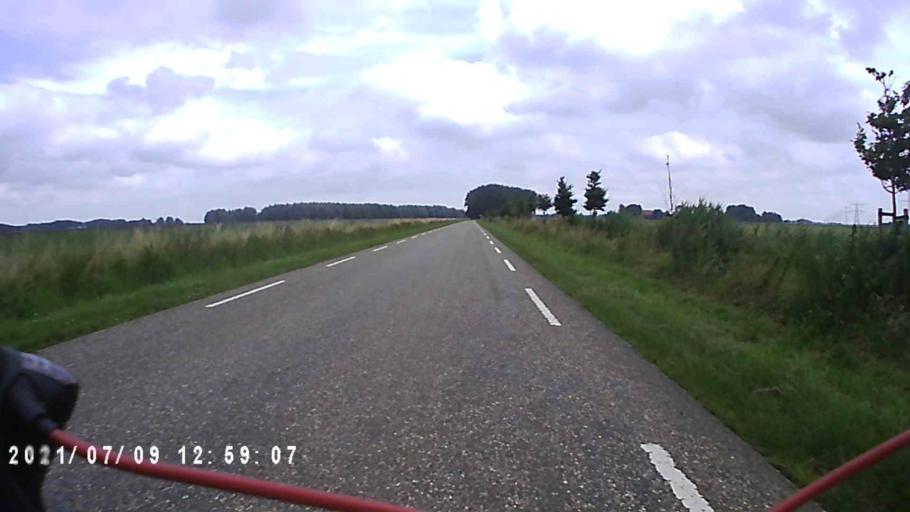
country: NL
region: Groningen
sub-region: Gemeente  Oldambt
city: Winschoten
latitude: 53.1312
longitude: 7.0660
